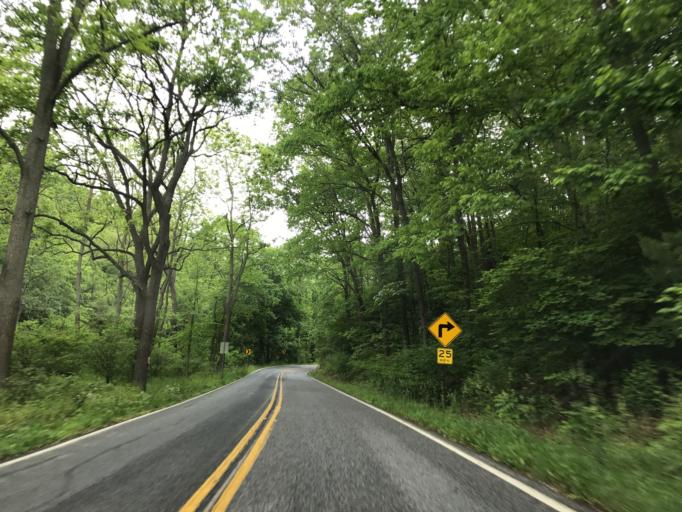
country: US
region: Pennsylvania
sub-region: York County
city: Loganville
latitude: 39.8409
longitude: -76.6648
